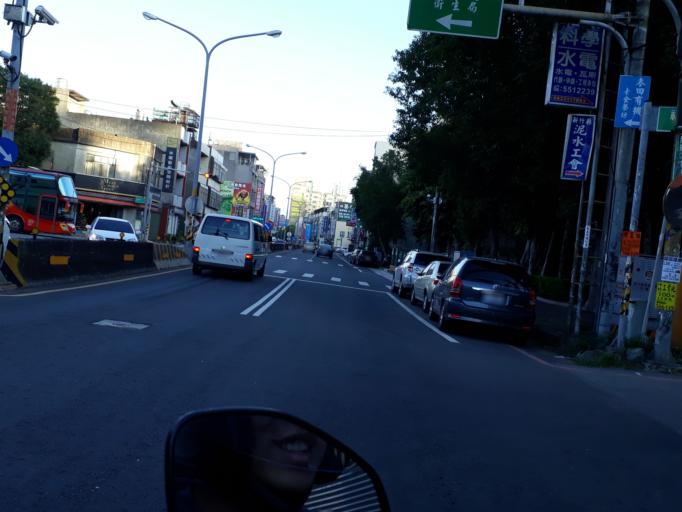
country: TW
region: Taiwan
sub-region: Hsinchu
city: Zhubei
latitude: 24.8230
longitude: 121.0100
